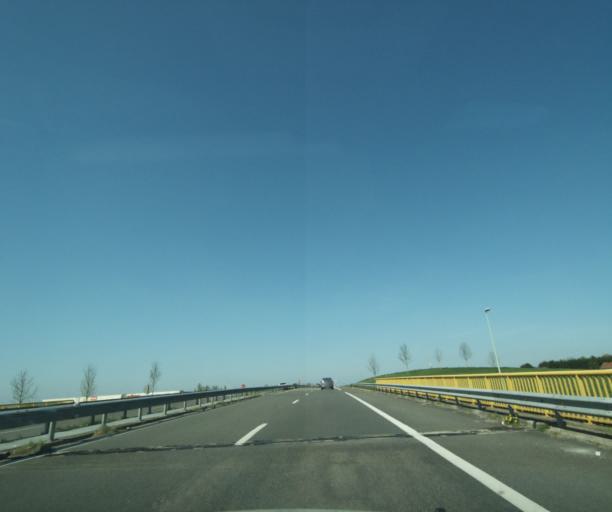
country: FR
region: Bourgogne
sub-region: Departement de la Nievre
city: Cosne-Cours-sur-Loire
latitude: 47.3825
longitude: 2.9231
